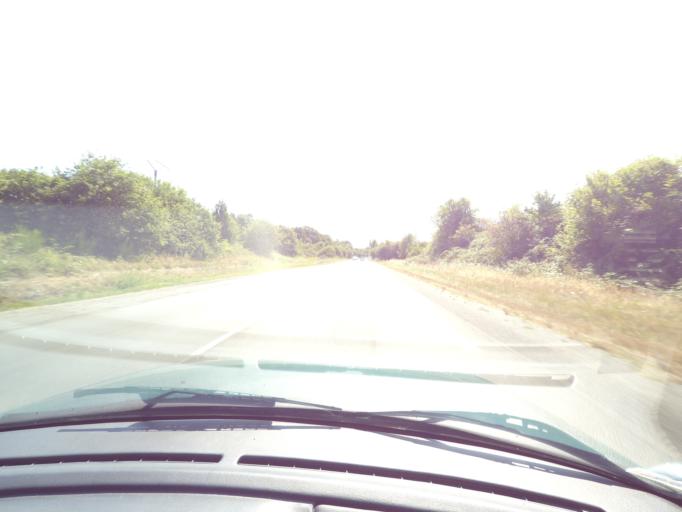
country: FR
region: Limousin
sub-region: Departement de la Haute-Vienne
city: Chaptelat
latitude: 45.8981
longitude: 1.2414
